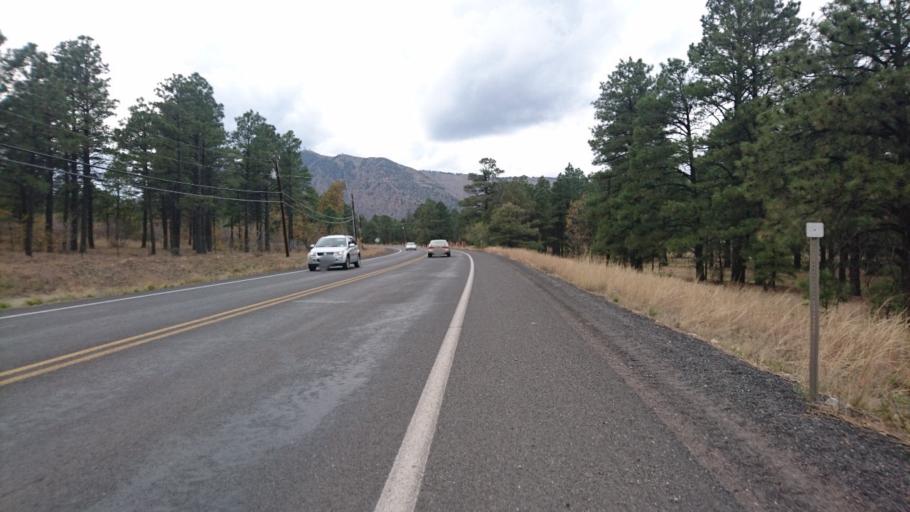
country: US
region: Arizona
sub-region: Coconino County
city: Flagstaff
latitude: 35.2463
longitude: -111.5539
